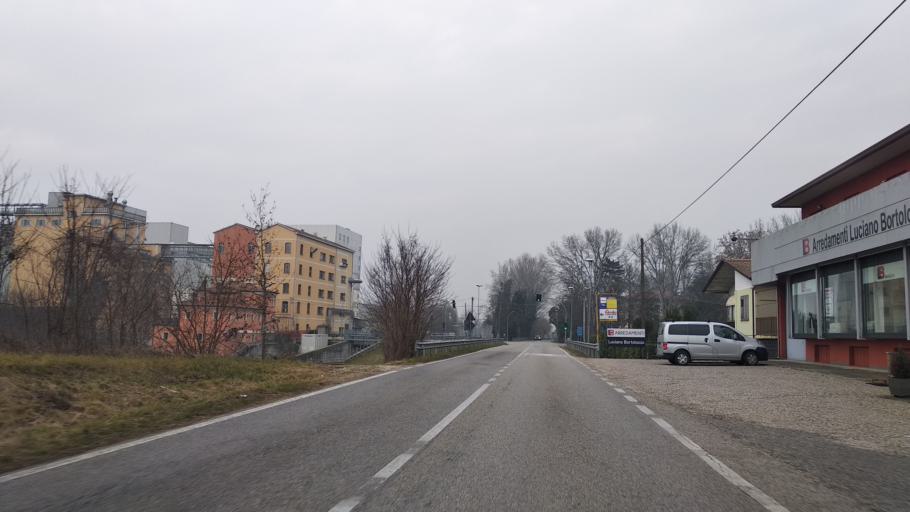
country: IT
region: Veneto
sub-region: Provincia di Padova
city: Santa Maria di Non
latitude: 45.5136
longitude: 11.8647
